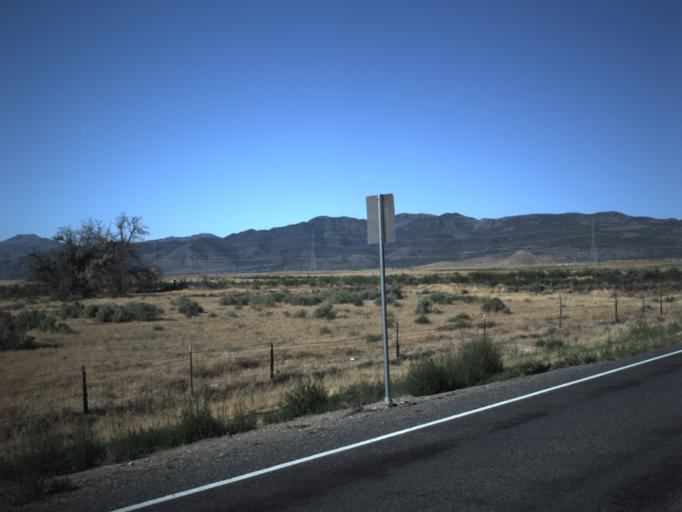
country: US
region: Utah
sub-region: Utah County
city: Genola
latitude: 39.9519
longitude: -111.9623
